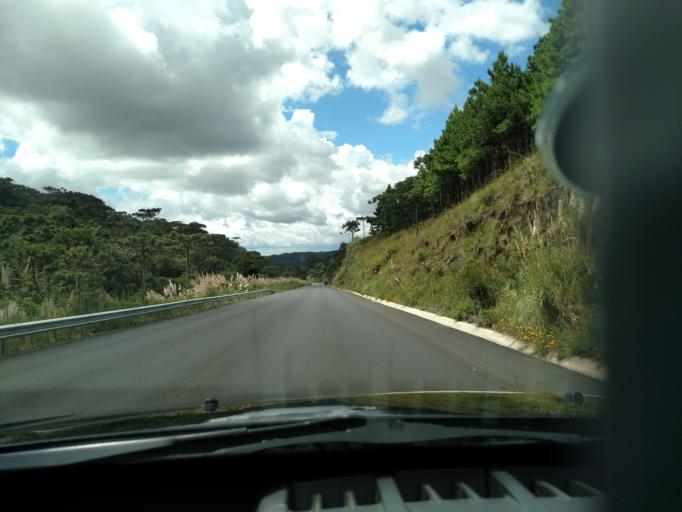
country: BR
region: Santa Catarina
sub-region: Lages
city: Lages
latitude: -27.9647
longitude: -50.0988
